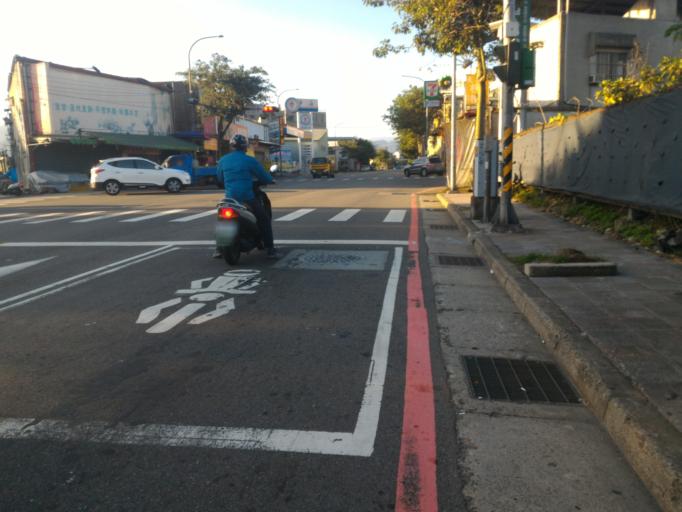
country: TW
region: Taiwan
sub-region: Taoyuan
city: Taoyuan
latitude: 24.9631
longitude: 121.3916
